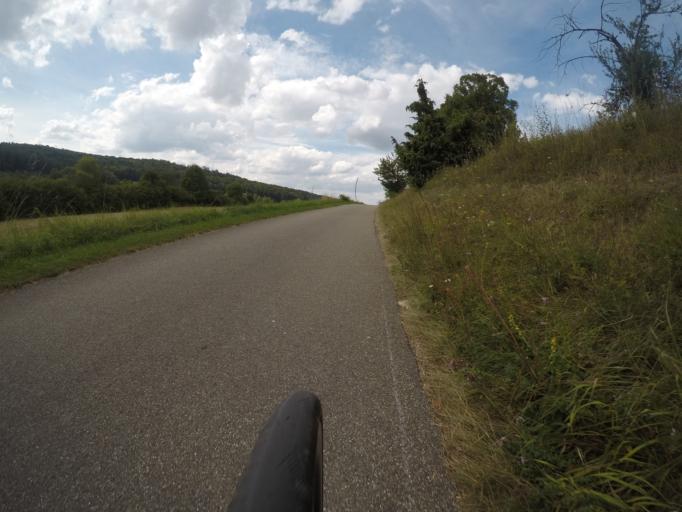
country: DE
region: Baden-Wuerttemberg
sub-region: Regierungsbezirk Stuttgart
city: Weil der Stadt
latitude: 48.7292
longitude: 8.8844
